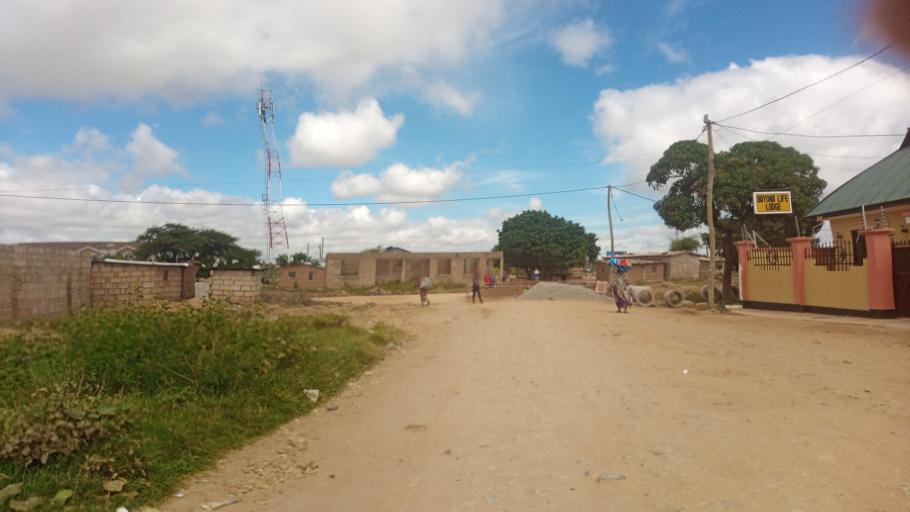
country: TZ
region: Dodoma
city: Dodoma
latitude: -6.1757
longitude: 35.7652
